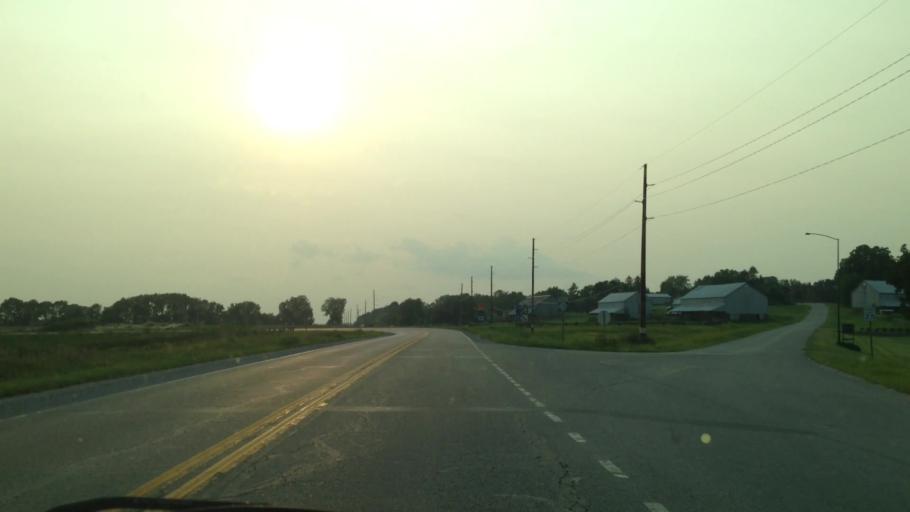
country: US
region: Iowa
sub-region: Iowa County
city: Marengo
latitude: 41.8051
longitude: -91.9591
